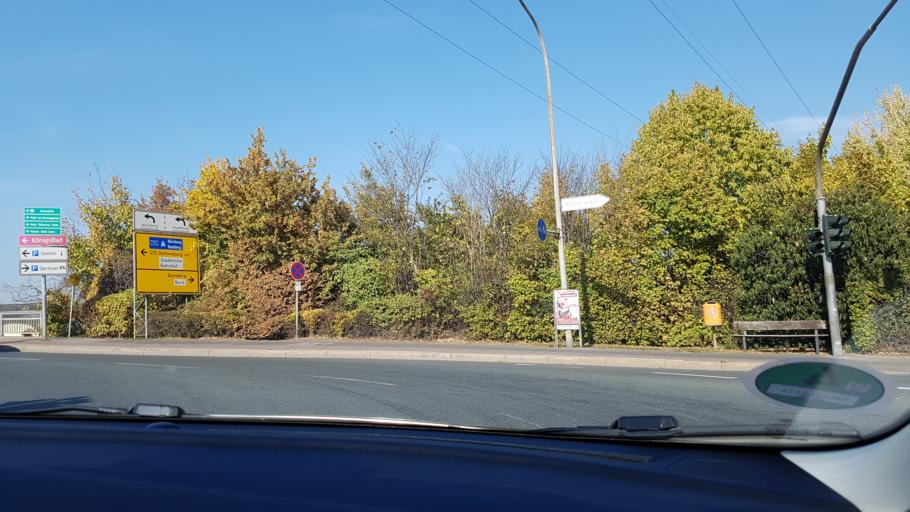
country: DE
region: Bavaria
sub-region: Upper Franconia
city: Forchheim
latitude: 49.7191
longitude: 11.0701
